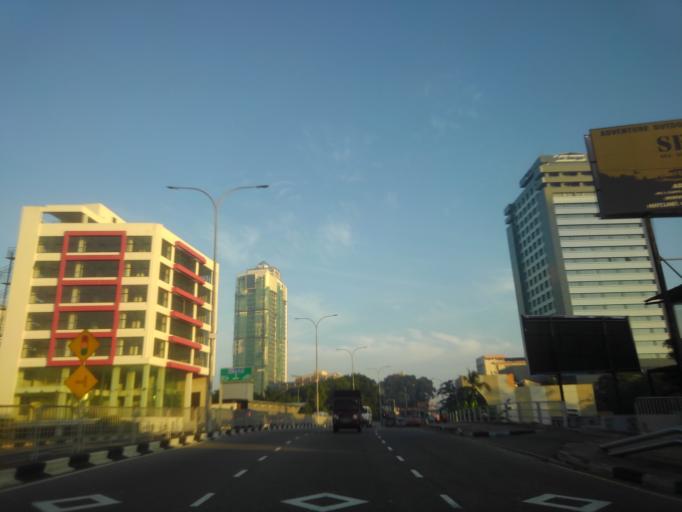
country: LK
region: Western
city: Pita Kotte
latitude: 6.8878
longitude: 79.8770
